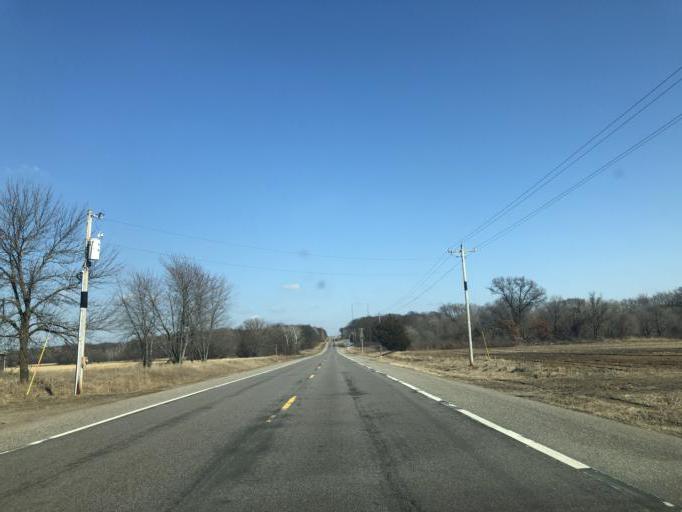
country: US
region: Minnesota
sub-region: Sherburne County
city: Becker
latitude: 45.4298
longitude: -93.8574
